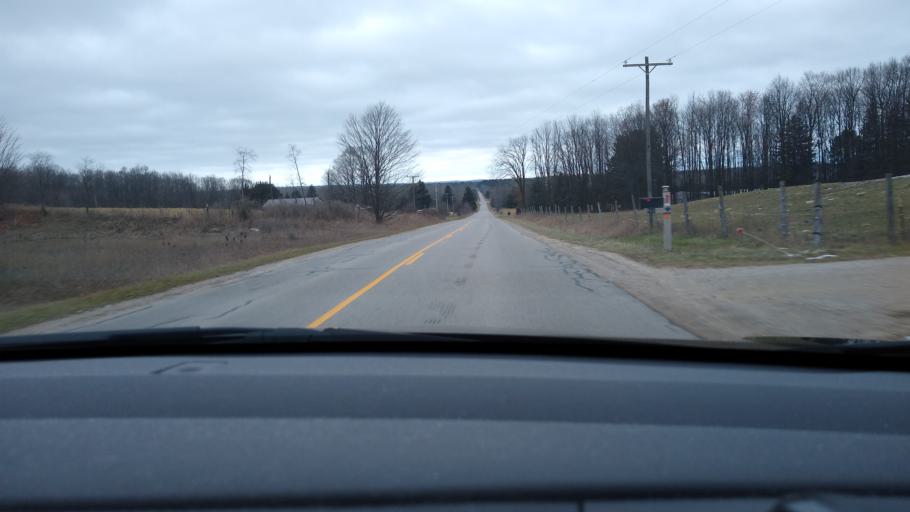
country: US
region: Michigan
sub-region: Missaukee County
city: Lake City
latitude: 44.3284
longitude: -85.0549
